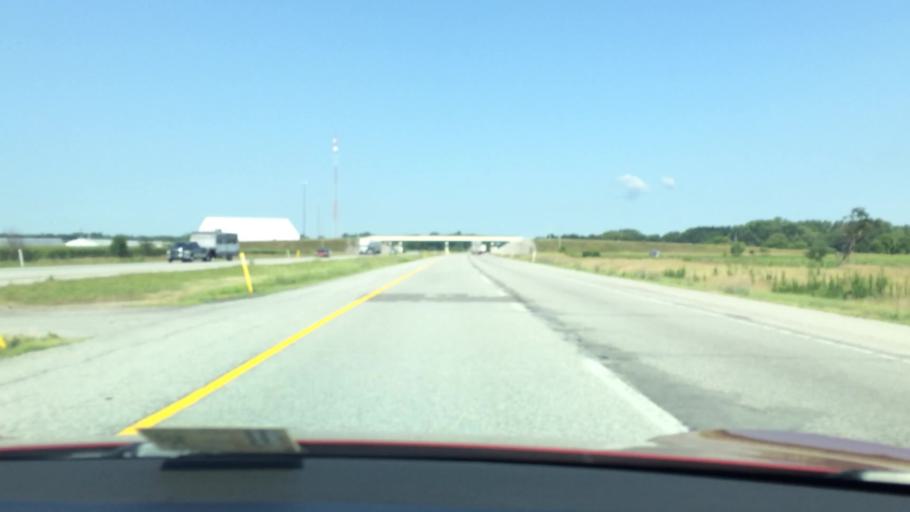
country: US
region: Michigan
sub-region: Saint Joseph County
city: White Pigeon
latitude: 41.7459
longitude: -85.5389
